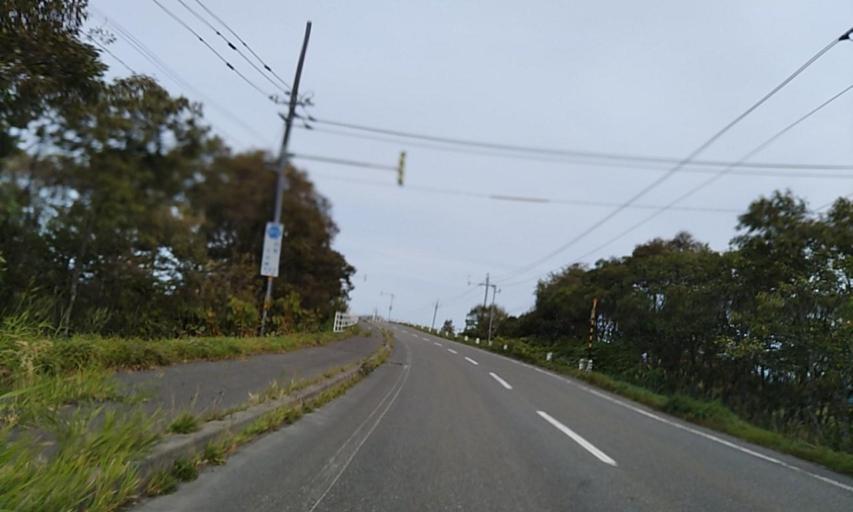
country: JP
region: Hokkaido
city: Makubetsu
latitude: 45.0033
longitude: 141.7067
